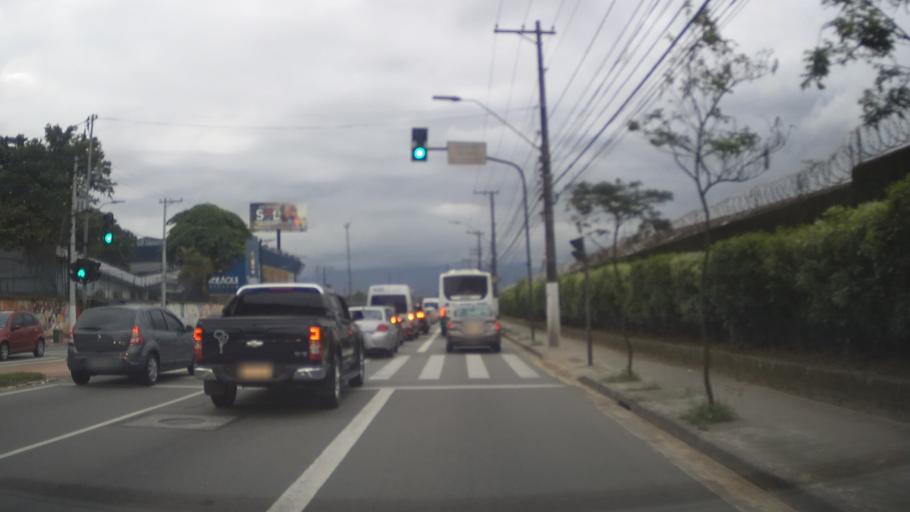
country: BR
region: Sao Paulo
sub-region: Santos
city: Santos
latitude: -23.9298
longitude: -46.3403
